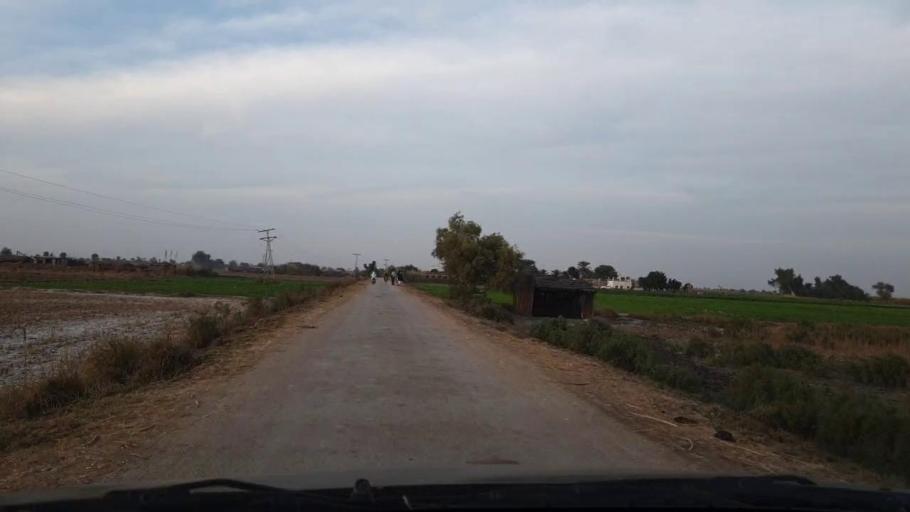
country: PK
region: Sindh
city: Khadro
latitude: 26.1350
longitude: 68.7570
